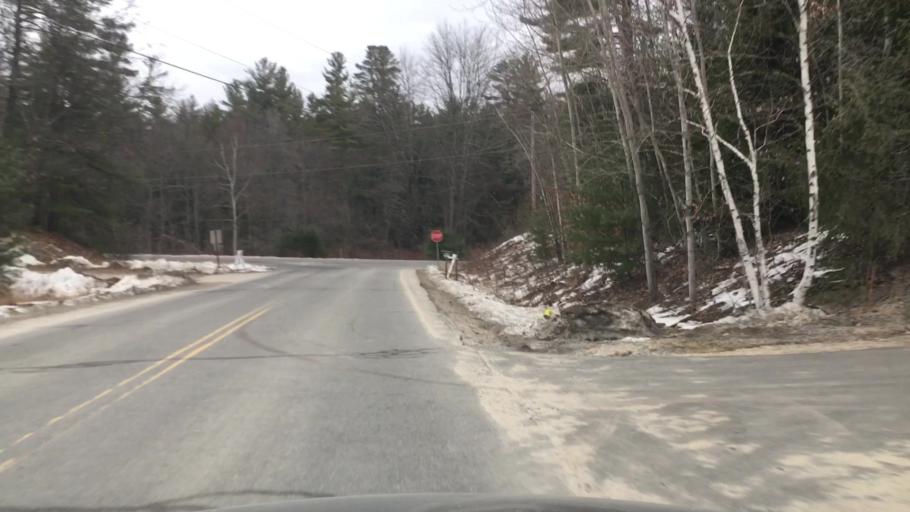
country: US
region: New Hampshire
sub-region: Hillsborough County
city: New Boston
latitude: 43.0003
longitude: -71.6617
